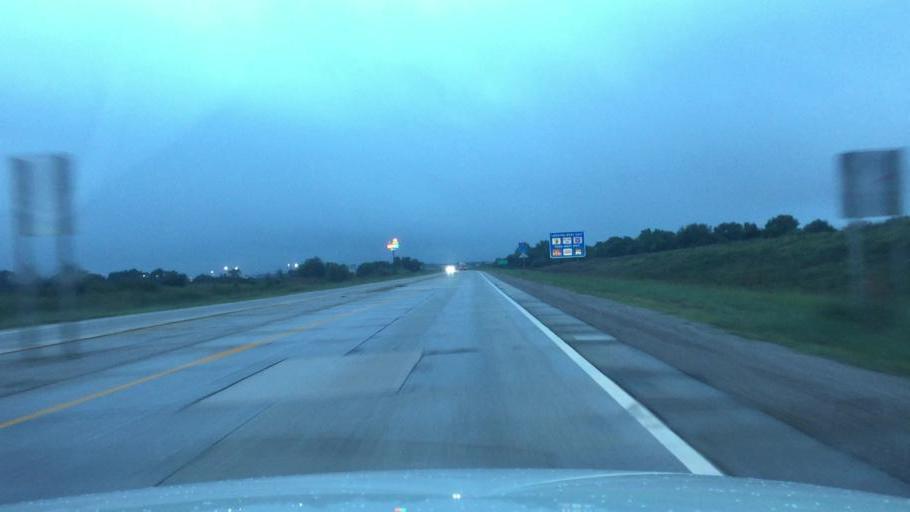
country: US
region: Kansas
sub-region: Neosho County
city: Chanute
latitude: 37.6582
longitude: -95.4796
